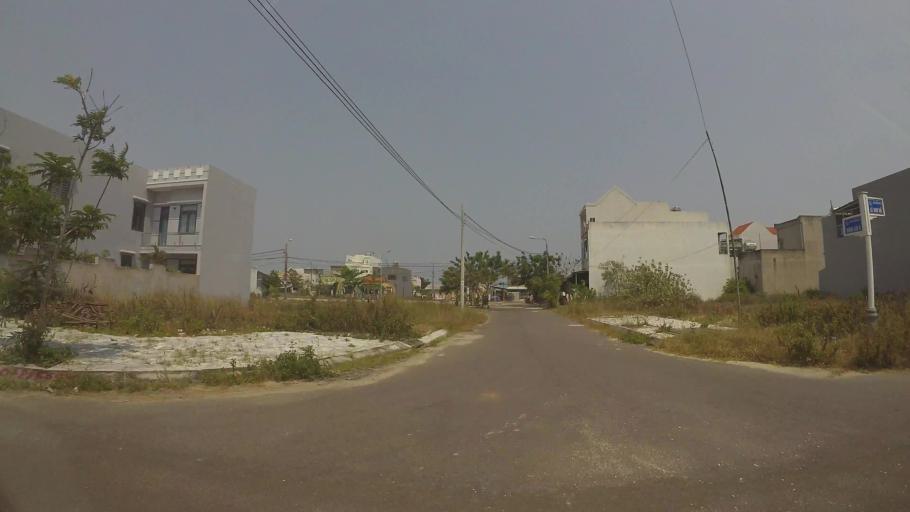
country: VN
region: Da Nang
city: Ngu Hanh Son
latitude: 15.9888
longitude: 108.2689
